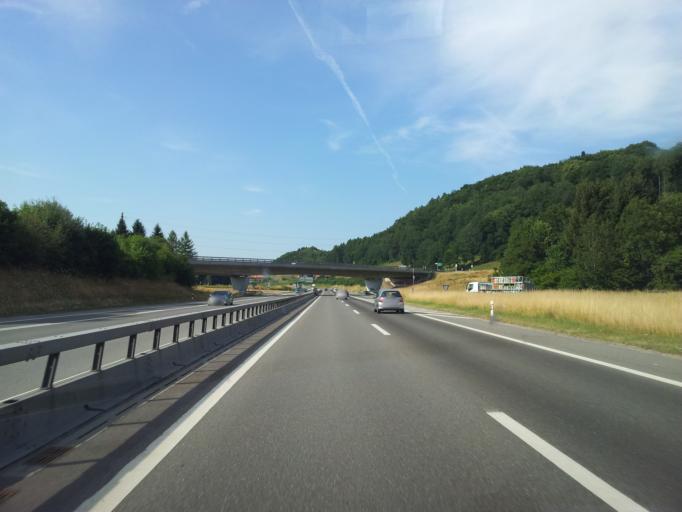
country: CH
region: Fribourg
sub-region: Veveyse District
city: Chatel-Saint-Denis
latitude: 46.5161
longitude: 6.9097
